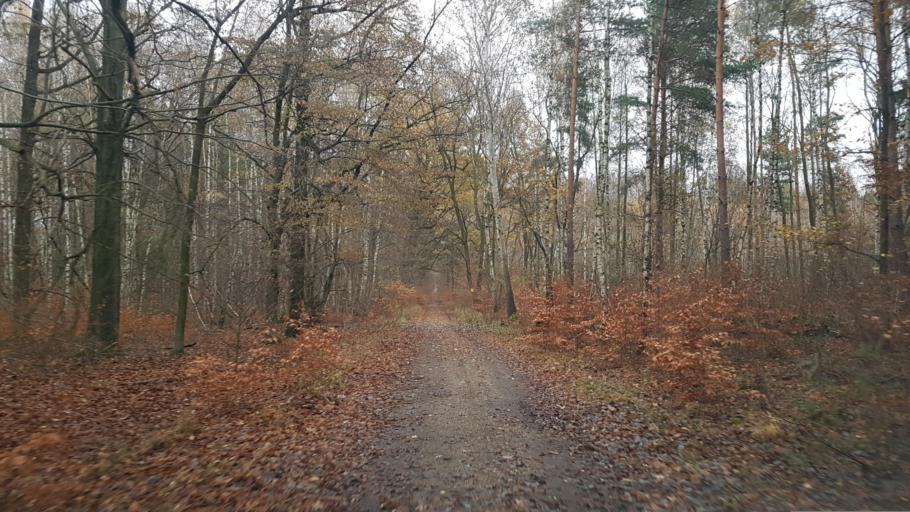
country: DE
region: Brandenburg
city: Crinitz
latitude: 51.7536
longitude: 13.7843
